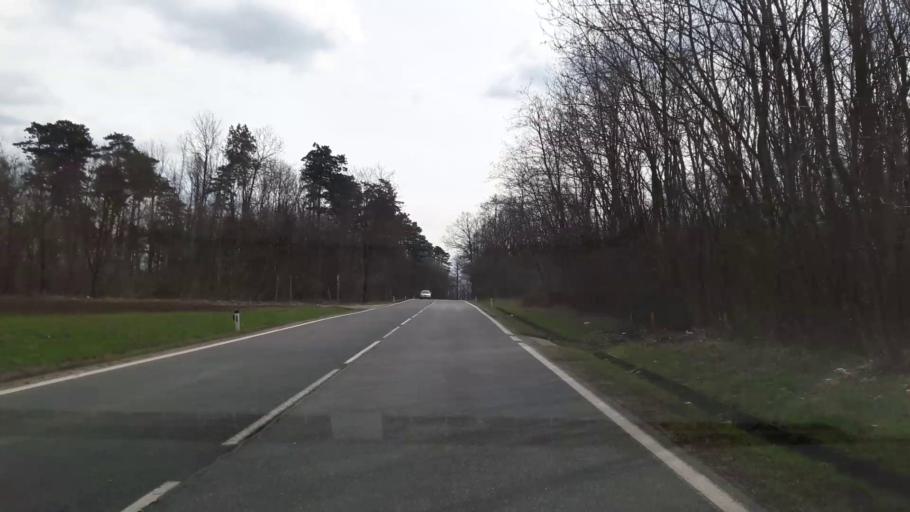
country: AT
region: Lower Austria
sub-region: Politischer Bezirk Mistelbach
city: Mistelbach
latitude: 48.5331
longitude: 16.6003
